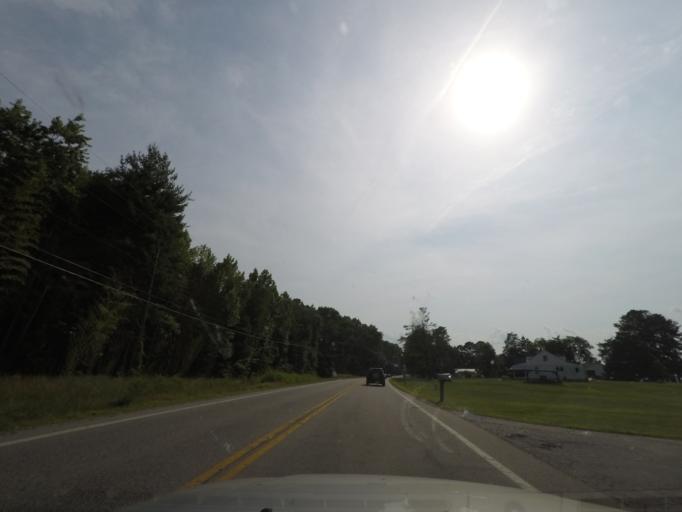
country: US
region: Virginia
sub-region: Prince Edward County
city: Hampden Sydney
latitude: 37.2534
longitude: -78.4208
